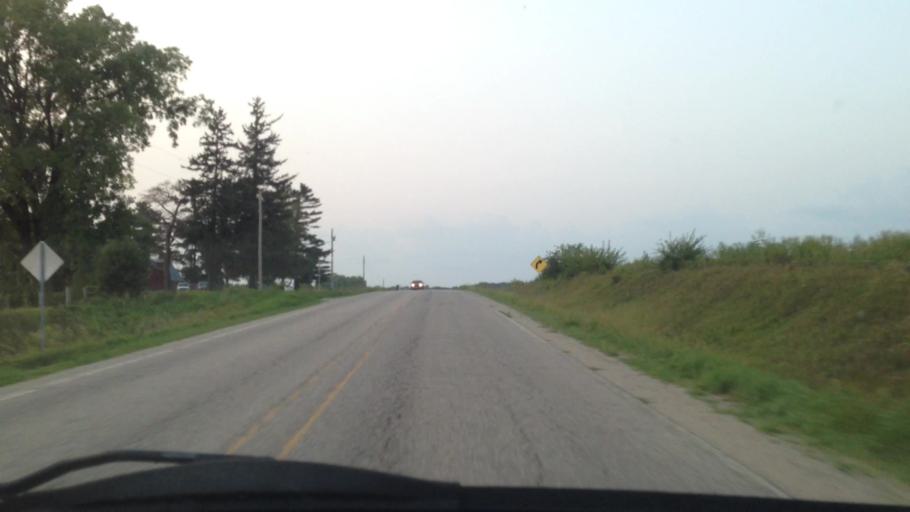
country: US
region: Iowa
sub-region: Benton County
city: Urbana
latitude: 42.1465
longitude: -91.8791
